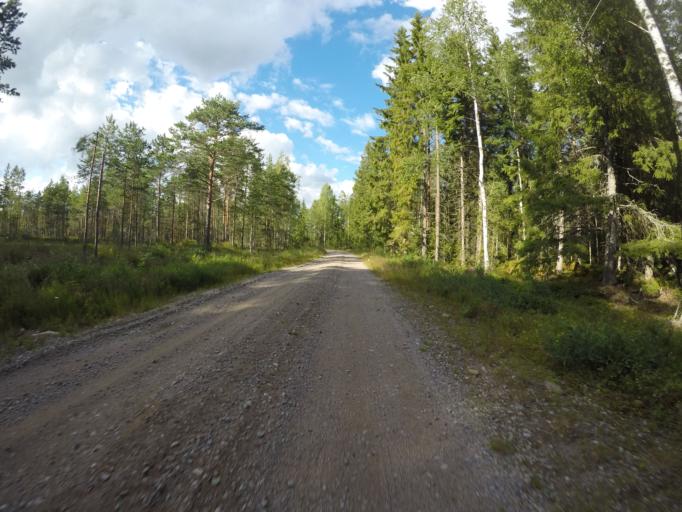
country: SE
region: OErebro
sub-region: Hallefors Kommun
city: Haellefors
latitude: 59.9460
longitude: 14.5637
